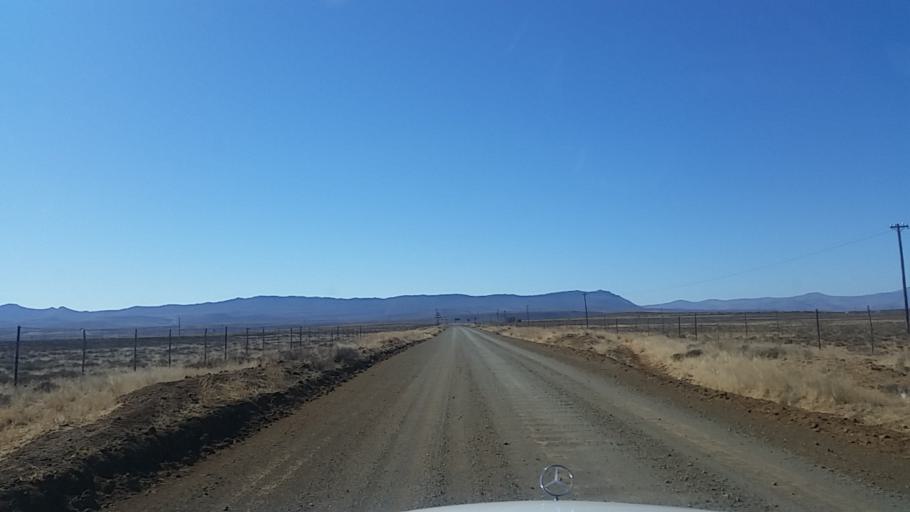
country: ZA
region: Eastern Cape
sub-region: Cacadu District Municipality
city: Graaff-Reinet
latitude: -31.9078
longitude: 24.7603
